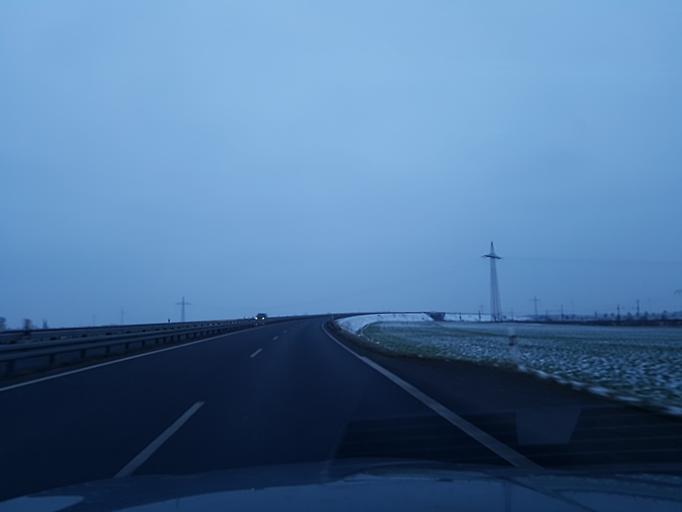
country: DE
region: Saxony
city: Riesa
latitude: 51.2917
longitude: 13.2775
